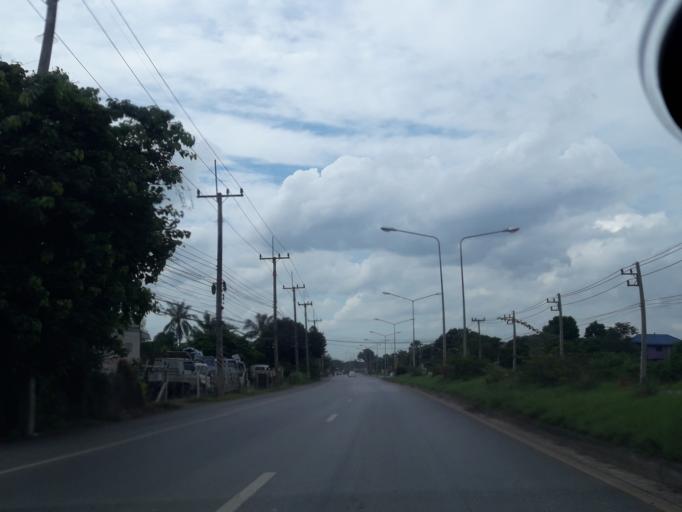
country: TH
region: Sara Buri
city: Kaeng Khoi
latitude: 14.5529
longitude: 101.0076
